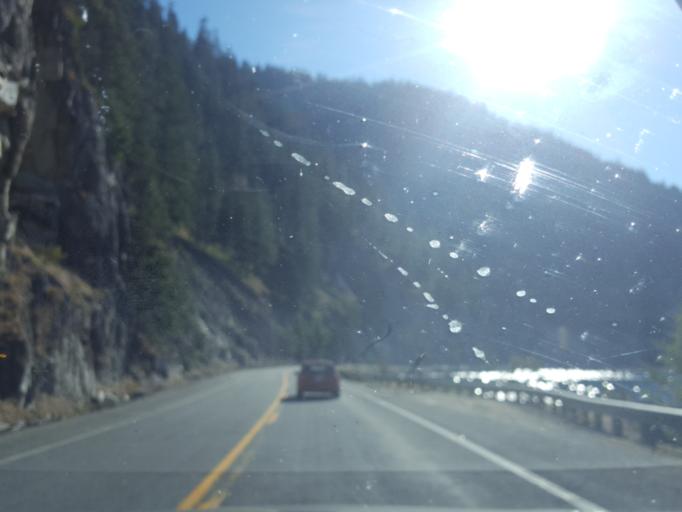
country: US
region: Washington
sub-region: Chelan County
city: Manson
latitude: 47.8603
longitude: -120.1602
